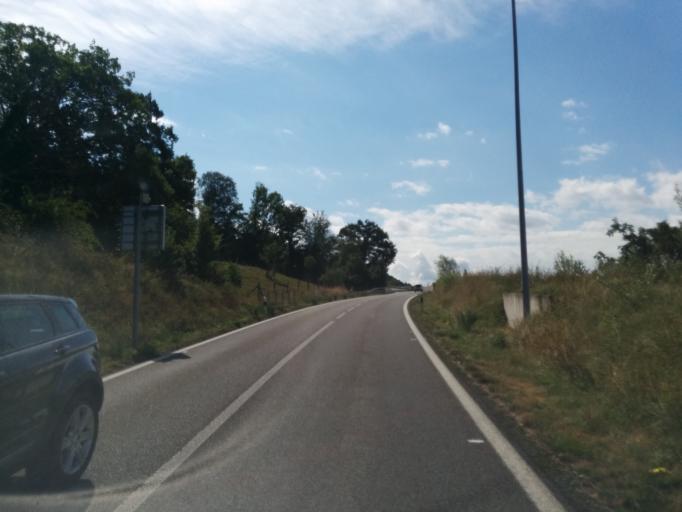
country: CH
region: Aargau
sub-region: Bezirk Bremgarten
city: Berikon
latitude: 47.3507
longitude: 8.3584
